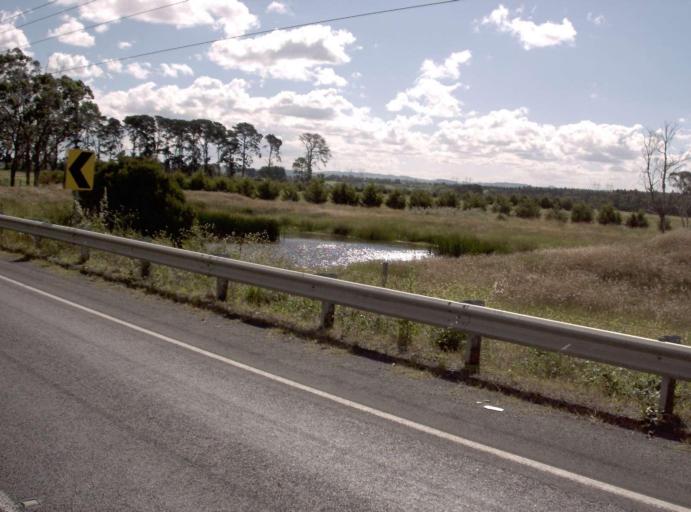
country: AU
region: Victoria
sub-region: Latrobe
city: Morwell
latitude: -38.2951
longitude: 146.4239
